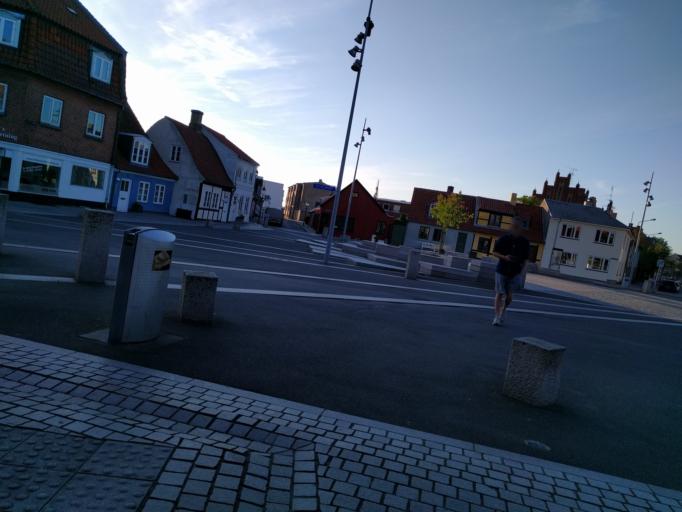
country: DK
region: Zealand
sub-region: Guldborgsund Kommune
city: Nykobing Falster
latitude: 54.7697
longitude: 11.8658
